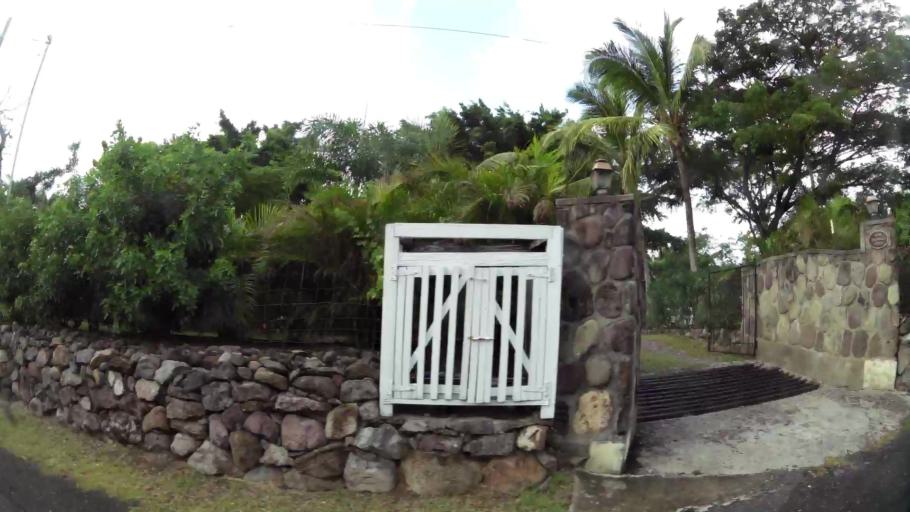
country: KN
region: Saint Thomas Lowland
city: Cotton Ground
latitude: 17.1937
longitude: -62.6151
